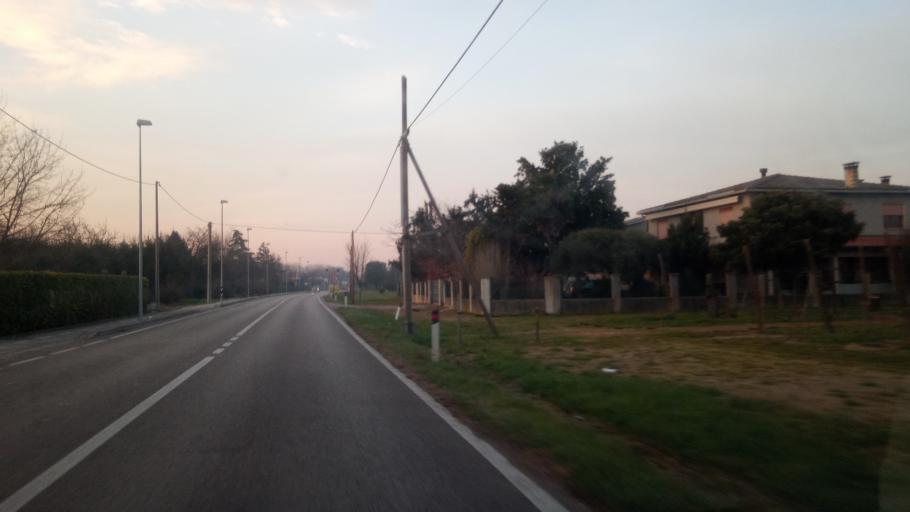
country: IT
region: Veneto
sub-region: Provincia di Padova
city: Saletto
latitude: 45.4664
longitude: 11.8680
